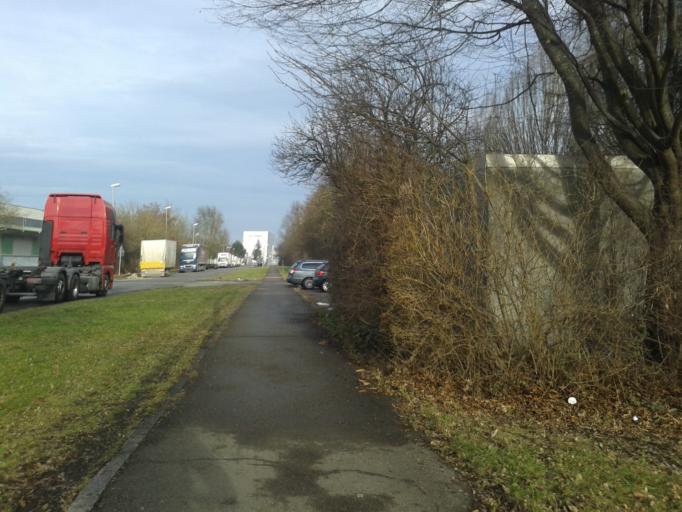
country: DE
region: Baden-Wuerttemberg
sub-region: Tuebingen Region
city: Erbach
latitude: 48.3637
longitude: 9.9383
